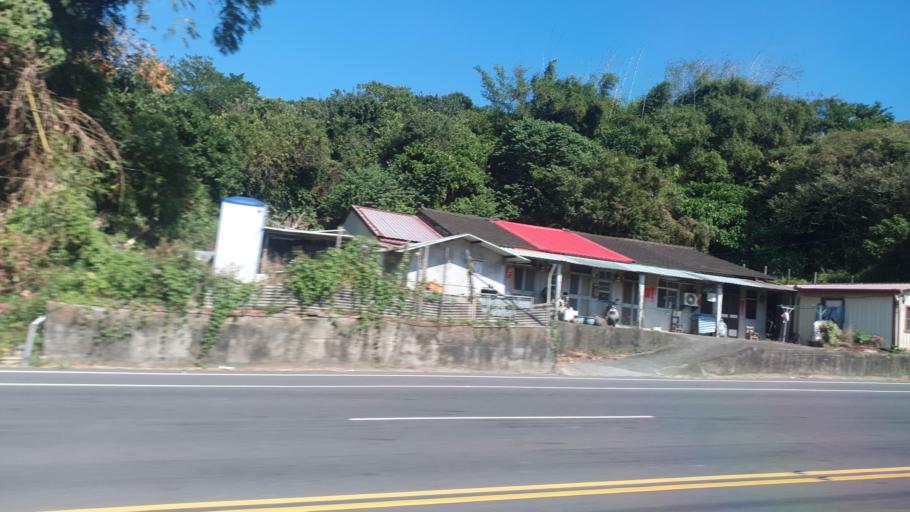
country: TW
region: Taiwan
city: Yujing
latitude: 23.0590
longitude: 120.3955
